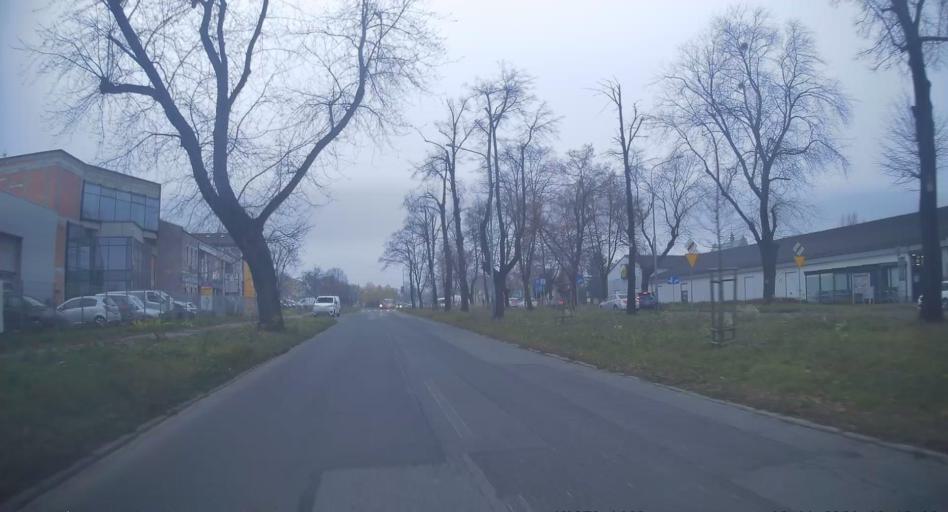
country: PL
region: Silesian Voivodeship
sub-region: Czestochowa
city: Czestochowa
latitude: 50.8167
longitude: 19.0996
